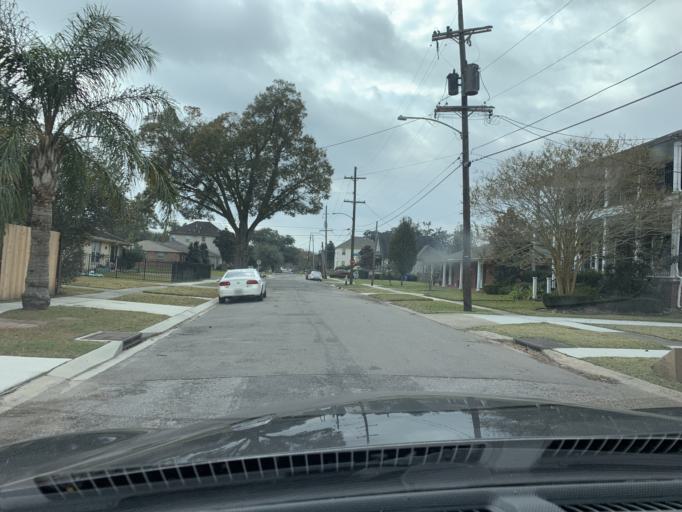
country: US
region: Louisiana
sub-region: Jefferson Parish
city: Metairie
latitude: 30.0189
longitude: -90.1041
